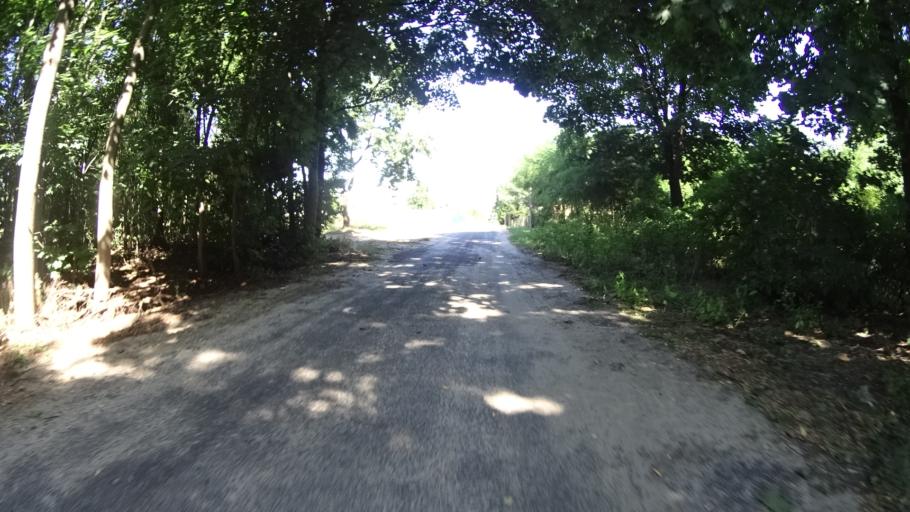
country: PL
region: Masovian Voivodeship
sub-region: Powiat bialobrzeski
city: Promna
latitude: 51.6703
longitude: 20.9319
